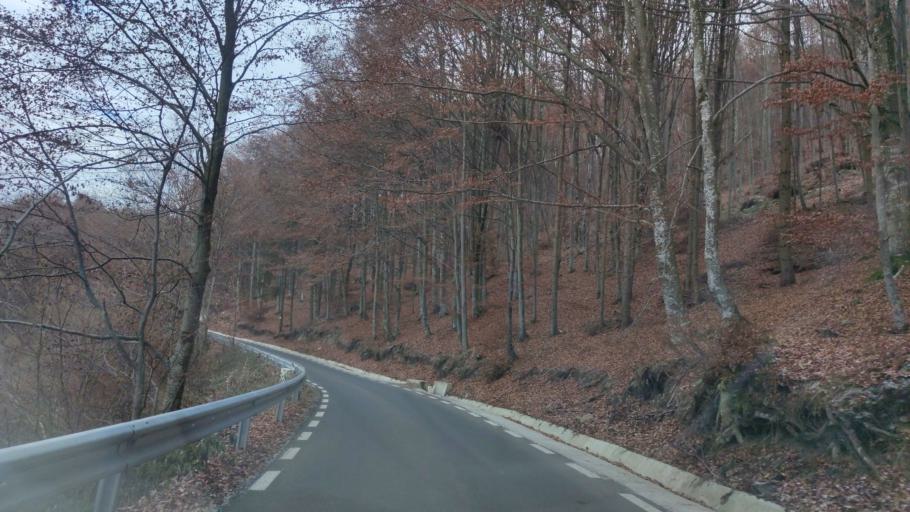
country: RO
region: Harghita
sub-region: Comuna Corund
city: Corund
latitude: 46.4815
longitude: 25.2244
